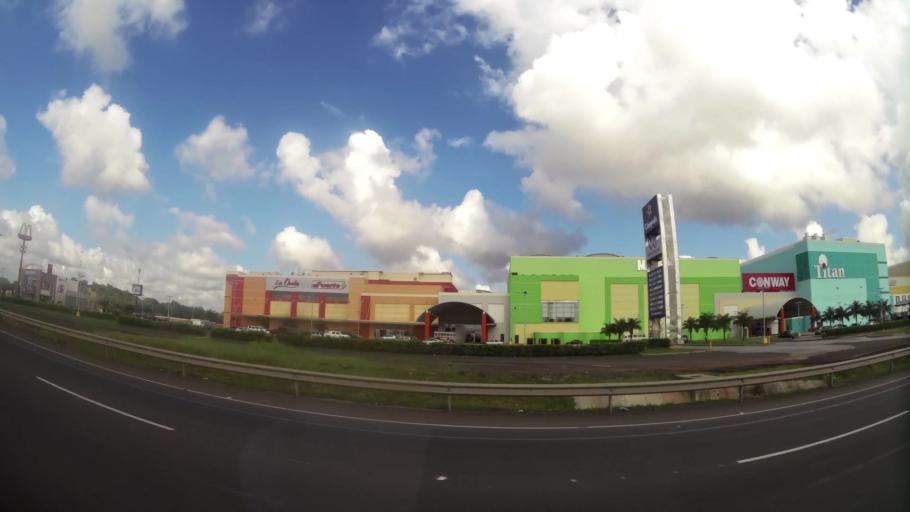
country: PA
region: Panama
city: Nuevo Arraijan
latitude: 8.9196
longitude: -79.7052
